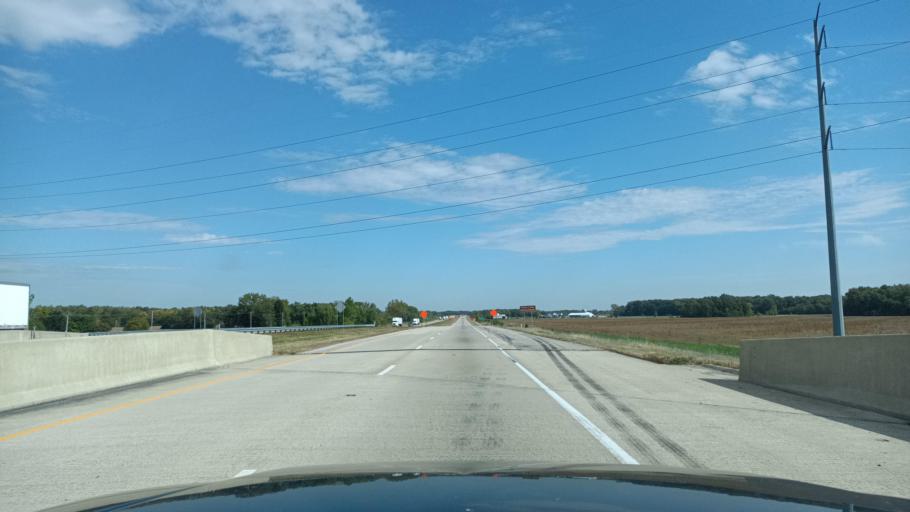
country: US
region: Indiana
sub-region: Allen County
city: New Haven
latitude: 41.0901
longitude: -84.9824
